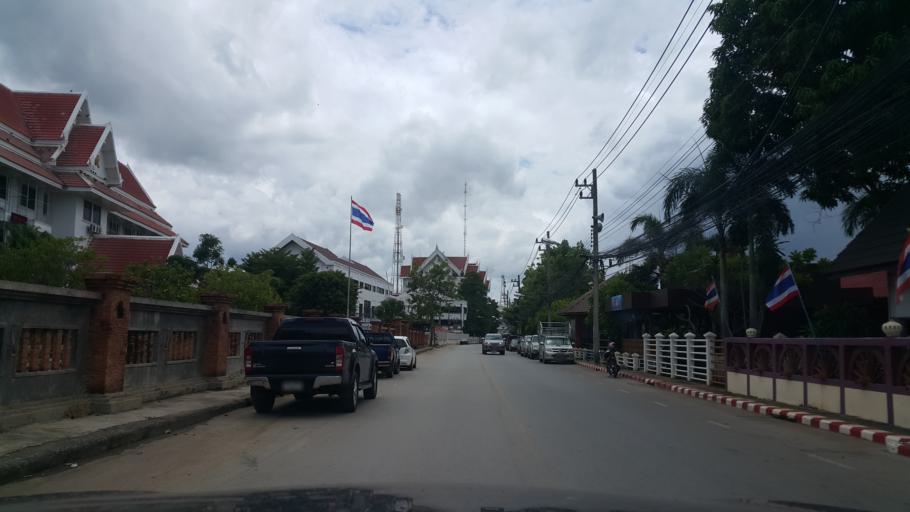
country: TH
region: Sukhothai
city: Sukhothai
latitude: 17.0052
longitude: 99.8292
